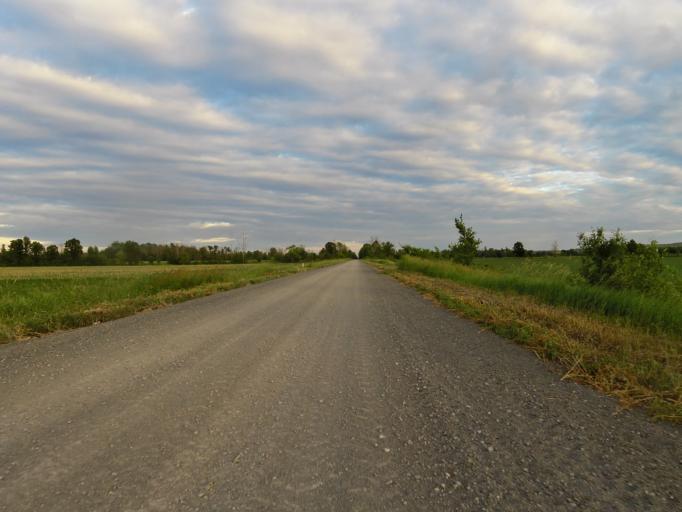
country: CA
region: Ontario
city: Arnprior
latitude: 45.3457
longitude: -76.3008
